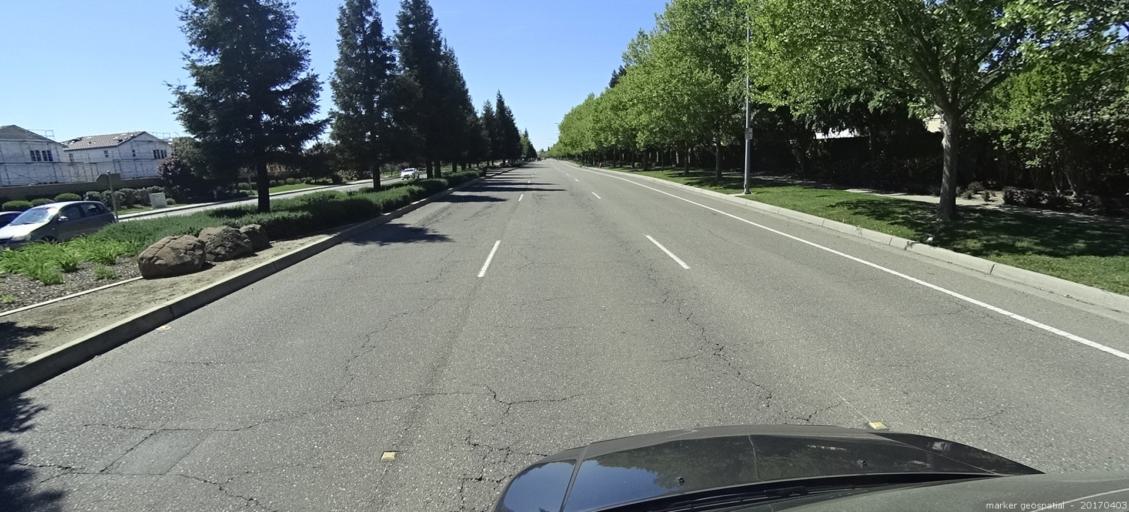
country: US
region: California
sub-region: Sacramento County
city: Rio Linda
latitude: 38.6563
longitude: -121.4971
